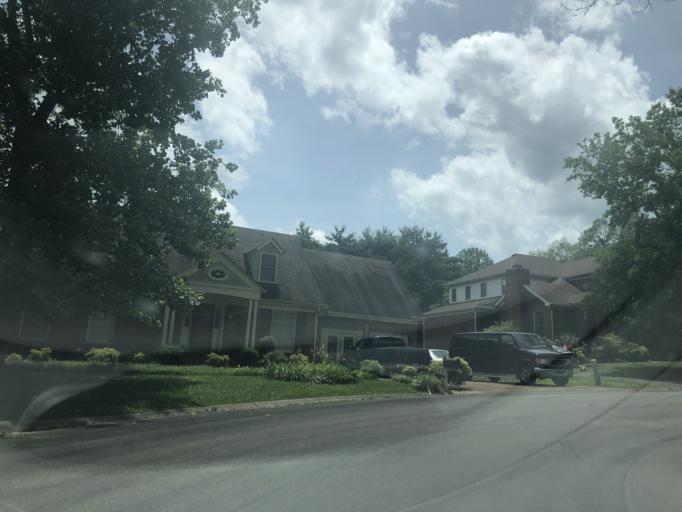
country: US
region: Tennessee
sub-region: Davidson County
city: Belle Meade
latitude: 36.0507
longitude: -86.9528
